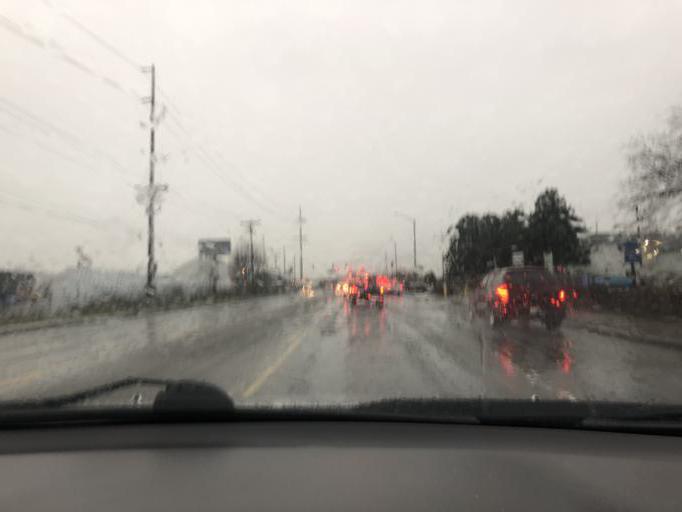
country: US
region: Washington
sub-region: Pierce County
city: Tacoma
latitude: 47.2477
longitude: -122.4146
